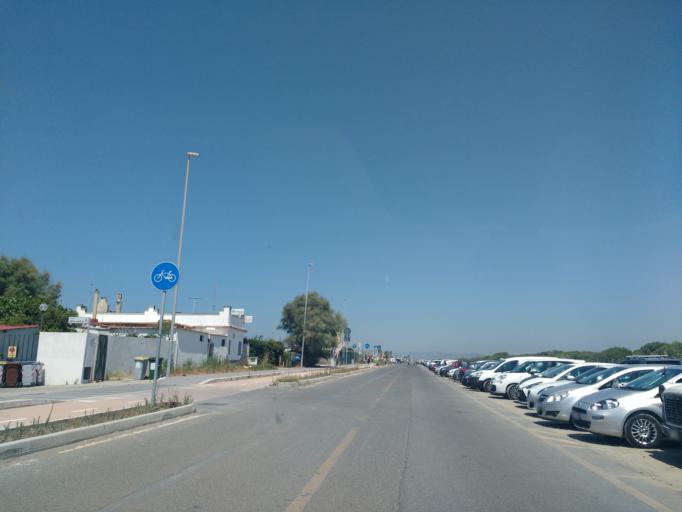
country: IT
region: Latium
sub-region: Citta metropolitana di Roma Capitale
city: Fregene
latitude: 41.8753
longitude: 12.1785
